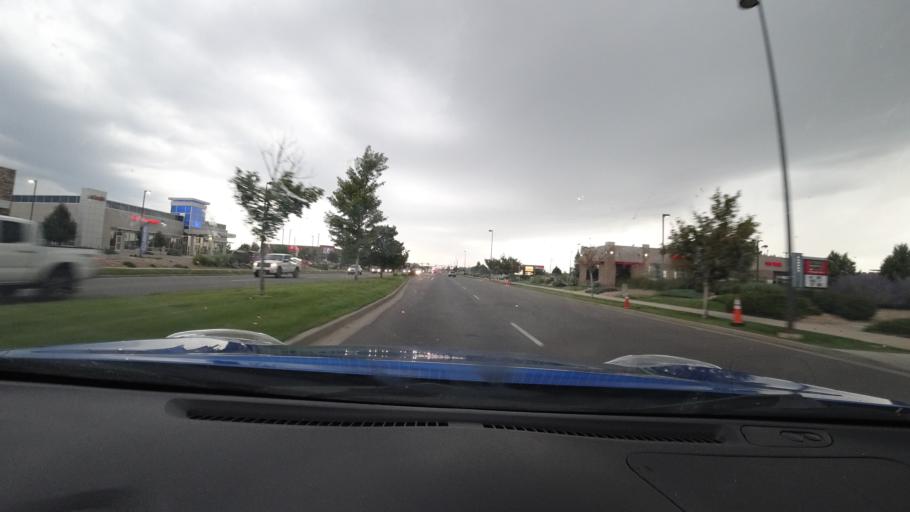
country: US
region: Colorado
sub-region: Adams County
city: Aurora
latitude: 39.7837
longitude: -104.7685
